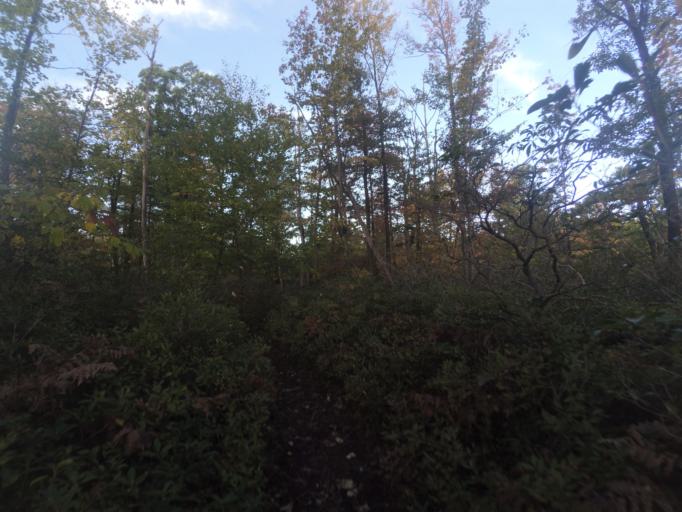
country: US
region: Pennsylvania
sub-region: Centre County
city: Stormstown
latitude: 40.8908
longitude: -77.9979
